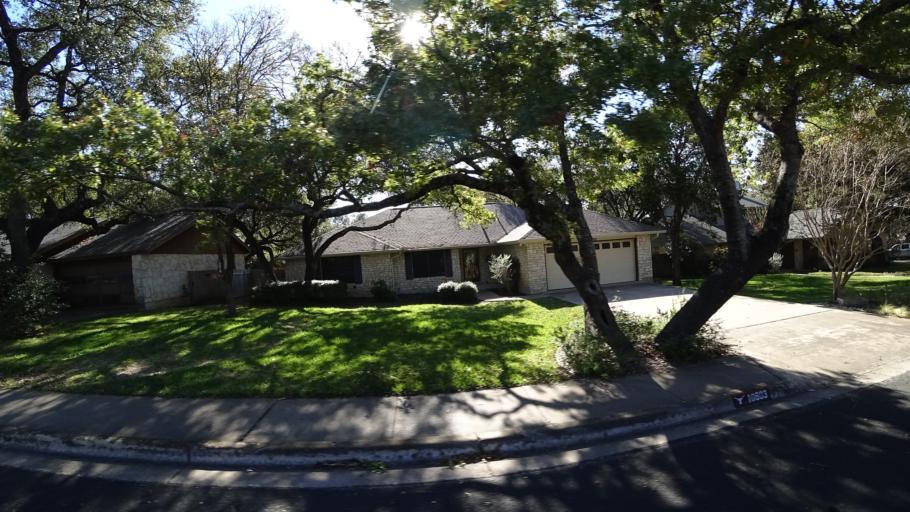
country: US
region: Texas
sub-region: Williamson County
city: Jollyville
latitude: 30.4177
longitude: -97.7708
